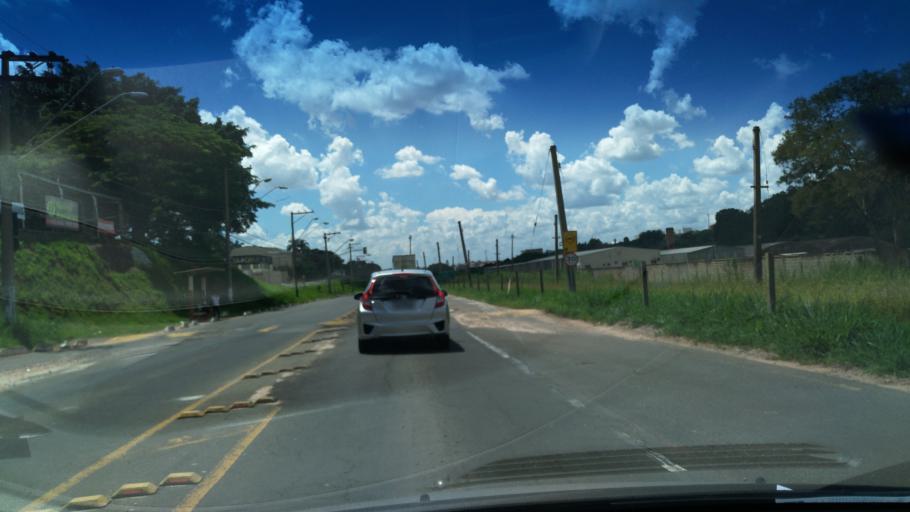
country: BR
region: Sao Paulo
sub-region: Valinhos
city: Valinhos
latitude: -22.9975
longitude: -46.9895
